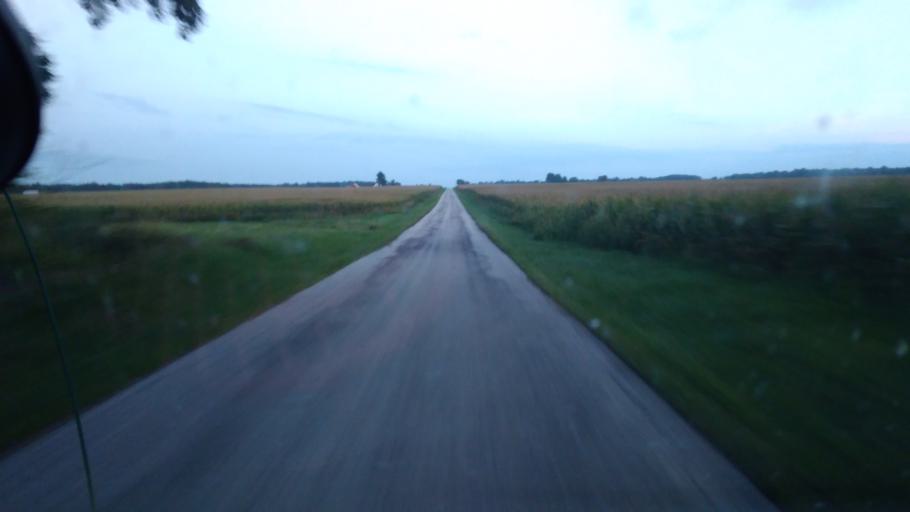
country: US
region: Ohio
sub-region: Hardin County
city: Kenton
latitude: 40.6518
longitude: -83.4586
